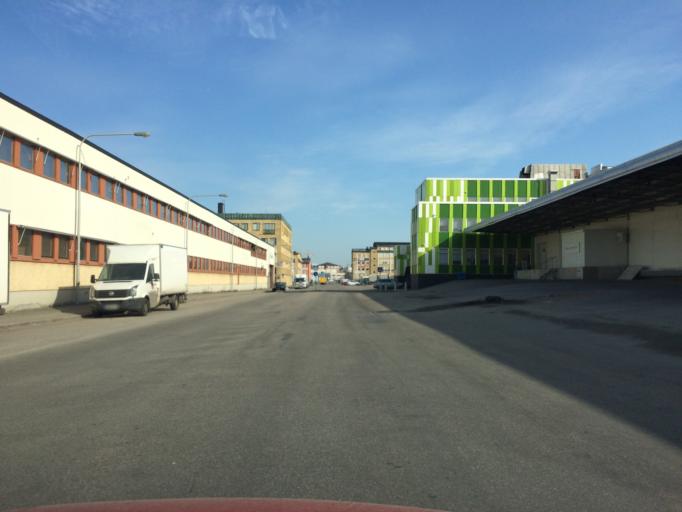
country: SE
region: Stockholm
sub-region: Stockholms Kommun
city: Arsta
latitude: 59.2962
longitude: 18.0136
